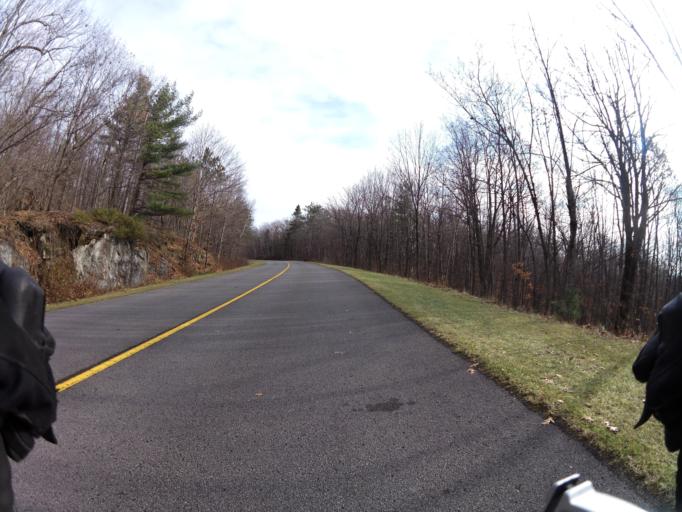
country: CA
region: Quebec
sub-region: Outaouais
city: Gatineau
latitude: 45.4660
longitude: -75.8125
